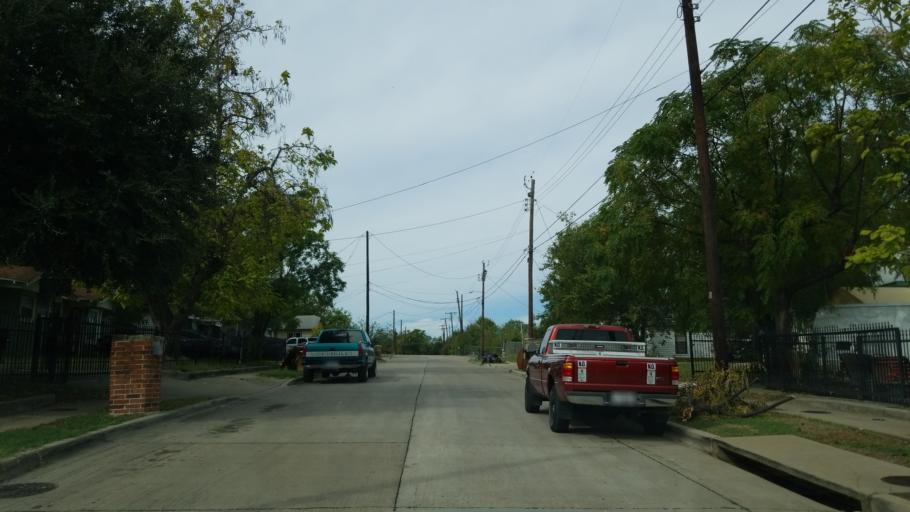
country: US
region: Texas
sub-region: Dallas County
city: Dallas
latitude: 32.7819
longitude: -96.7348
